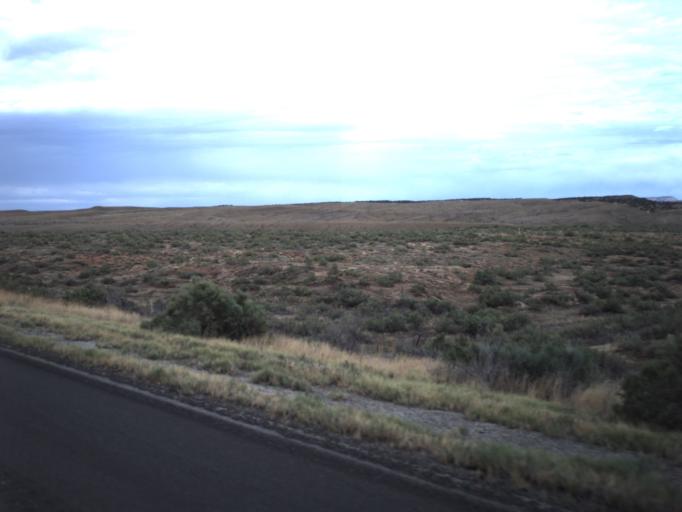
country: US
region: Colorado
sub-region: Mesa County
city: Loma
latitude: 39.0768
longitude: -109.2311
